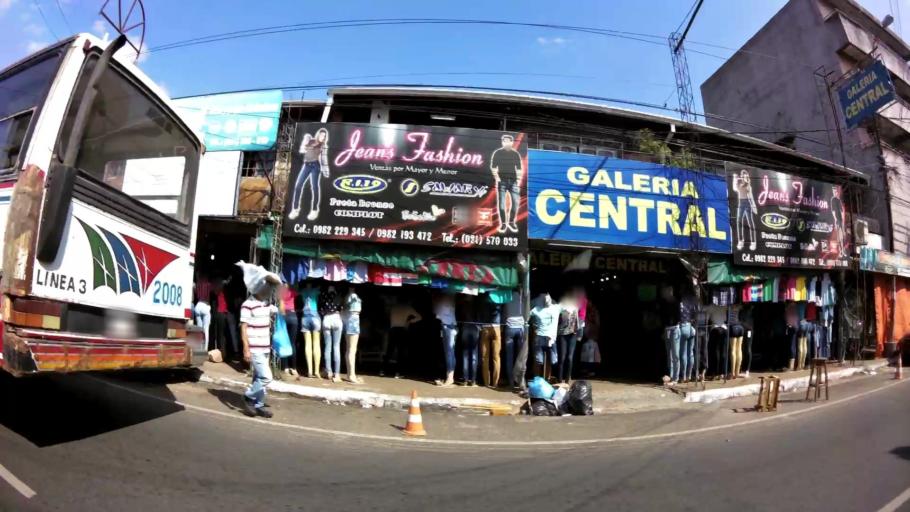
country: PY
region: Central
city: San Lorenzo
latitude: -25.3466
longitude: -57.5108
